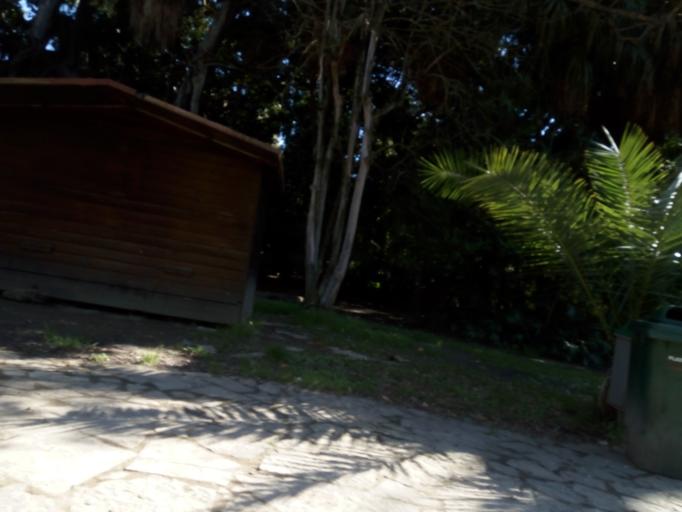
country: DZ
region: Alger
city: Algiers
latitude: 36.7477
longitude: 3.0778
